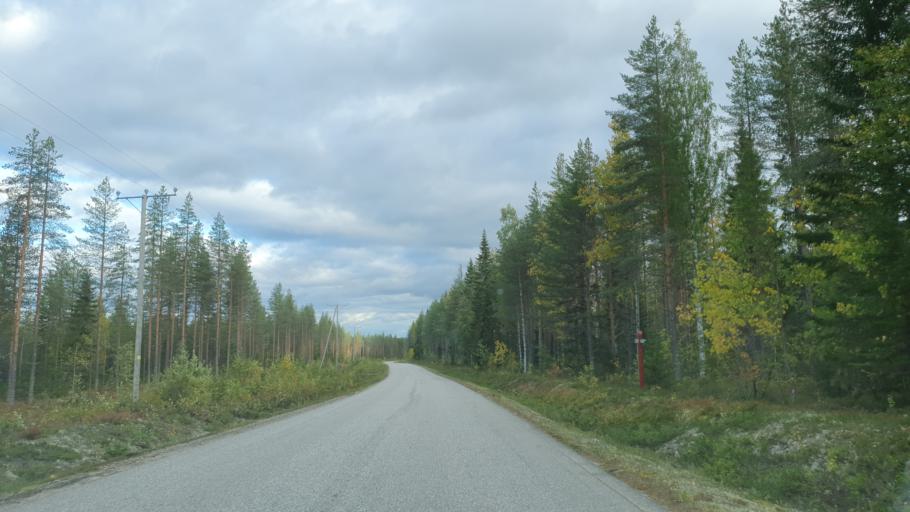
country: FI
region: Kainuu
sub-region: Kehys-Kainuu
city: Kuhmo
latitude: 63.9513
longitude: 29.8539
